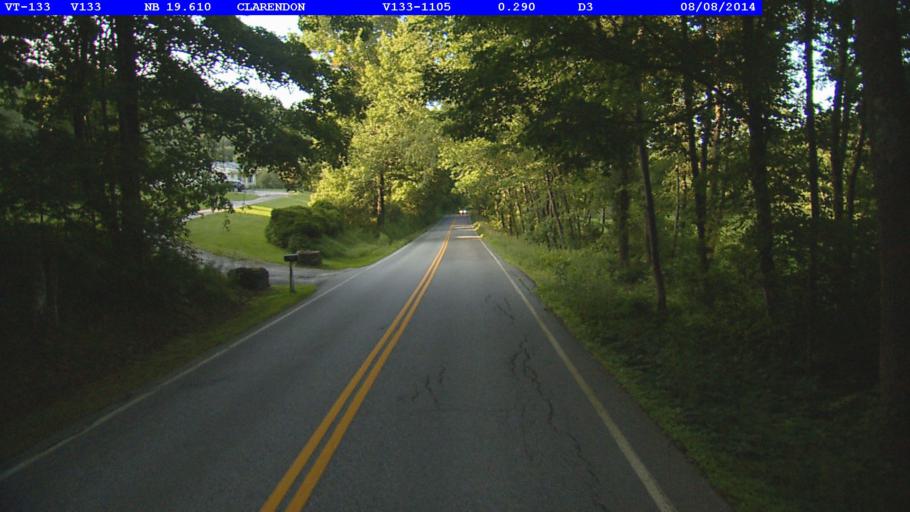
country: US
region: Vermont
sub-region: Rutland County
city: West Rutland
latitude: 43.5550
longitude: -73.0366
